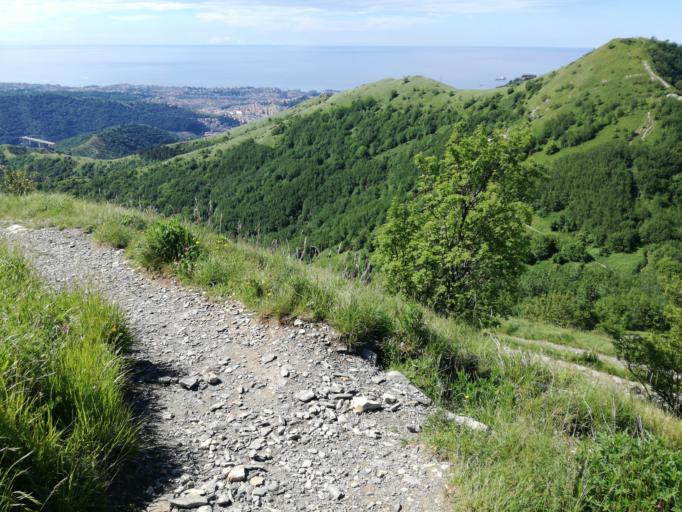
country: IT
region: Liguria
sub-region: Provincia di Genova
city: Manesseno
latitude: 44.4609
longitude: 8.9391
